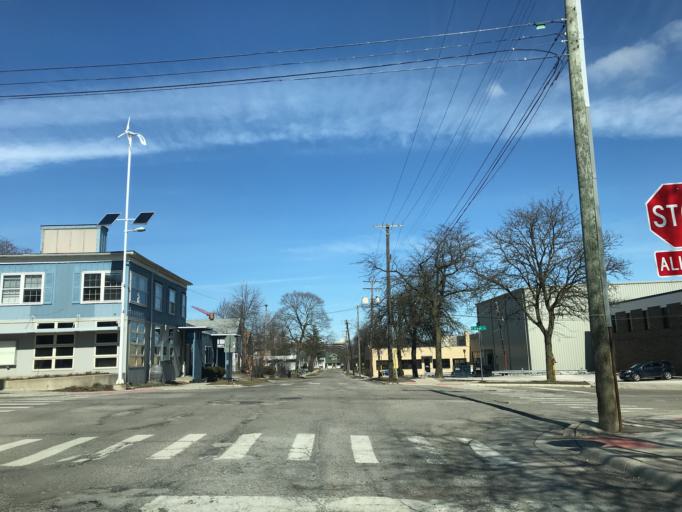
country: US
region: Michigan
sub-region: Washtenaw County
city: Ann Arbor
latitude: 42.2692
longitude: -83.7475
